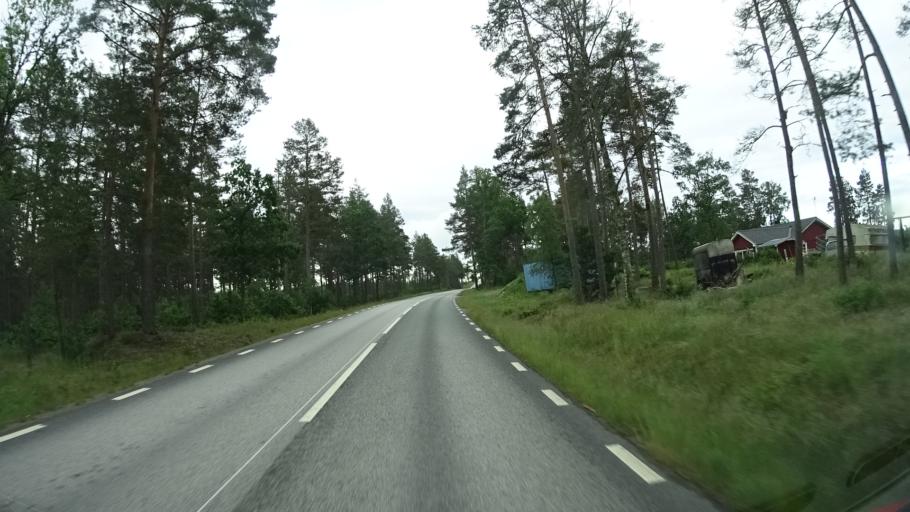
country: SE
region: Kalmar
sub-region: Oskarshamns Kommun
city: Oskarshamn
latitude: 57.3048
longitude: 16.2868
